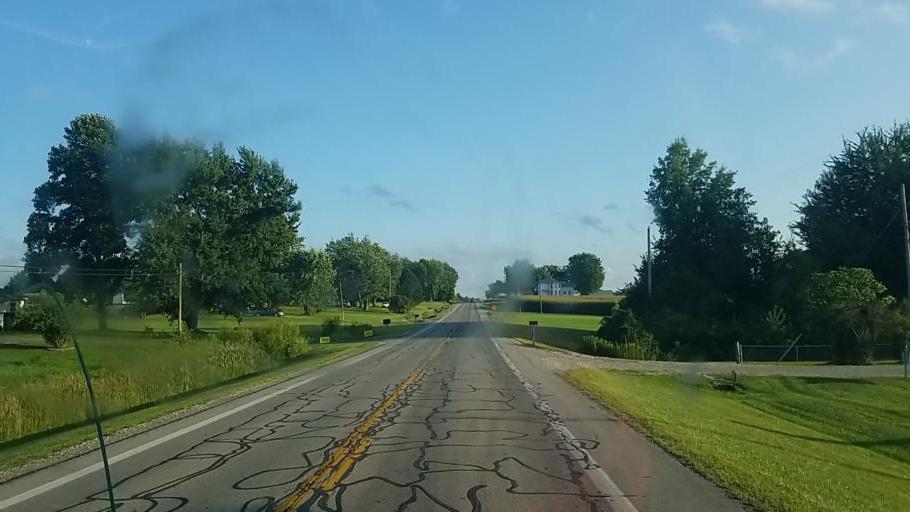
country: US
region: Ohio
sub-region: Crawford County
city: Galion
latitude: 40.6611
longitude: -82.8218
